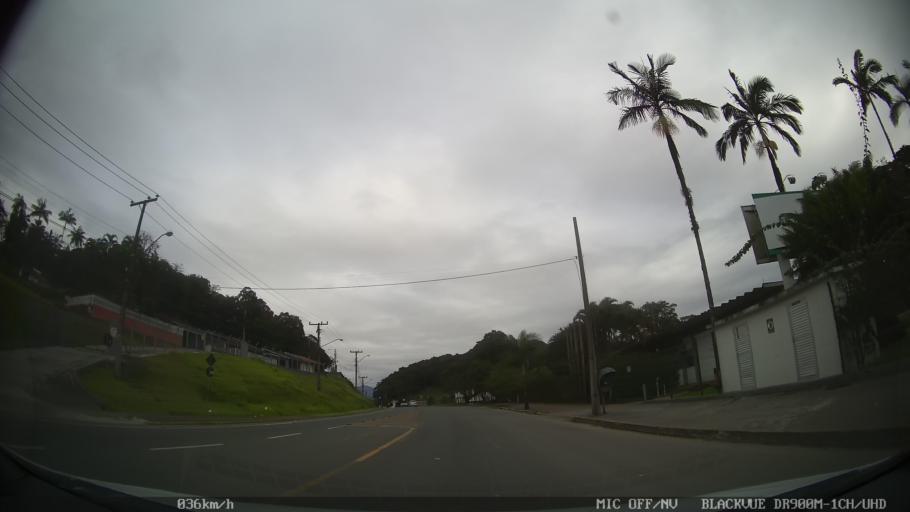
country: BR
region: Santa Catarina
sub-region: Joinville
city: Joinville
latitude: -26.2601
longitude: -48.8541
